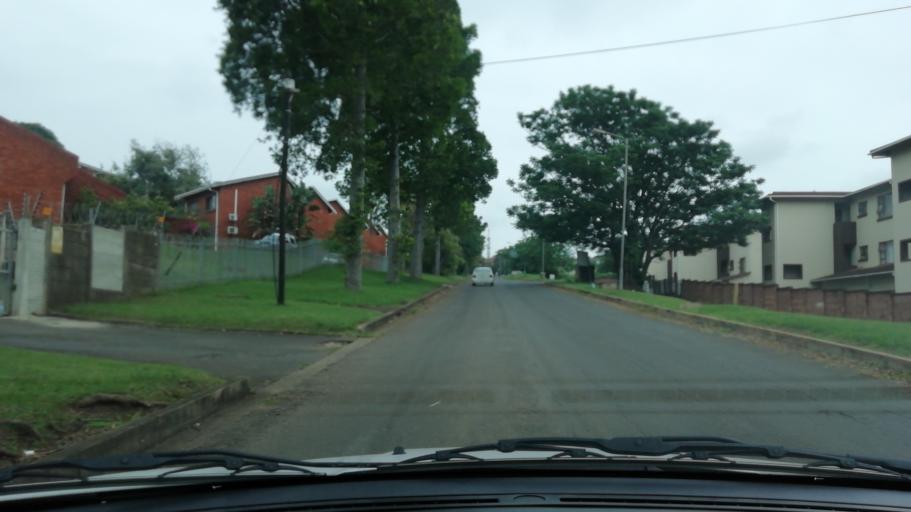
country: ZA
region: KwaZulu-Natal
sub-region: uThungulu District Municipality
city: Empangeni
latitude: -28.7391
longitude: 31.8861
